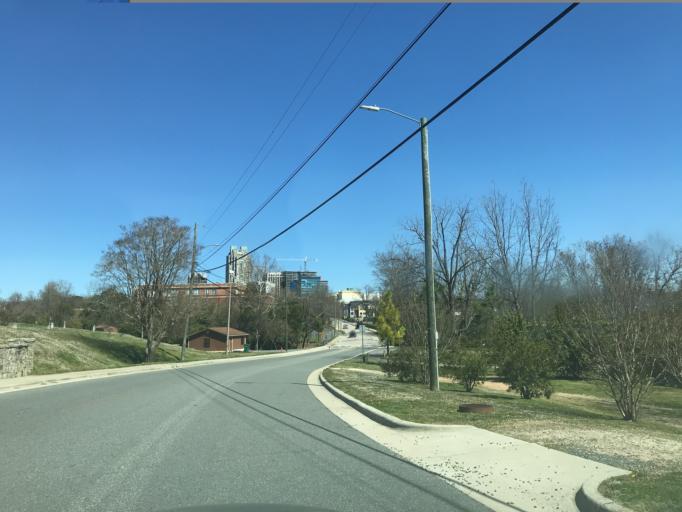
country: US
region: North Carolina
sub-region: Wake County
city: Raleigh
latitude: 35.7649
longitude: -78.6436
